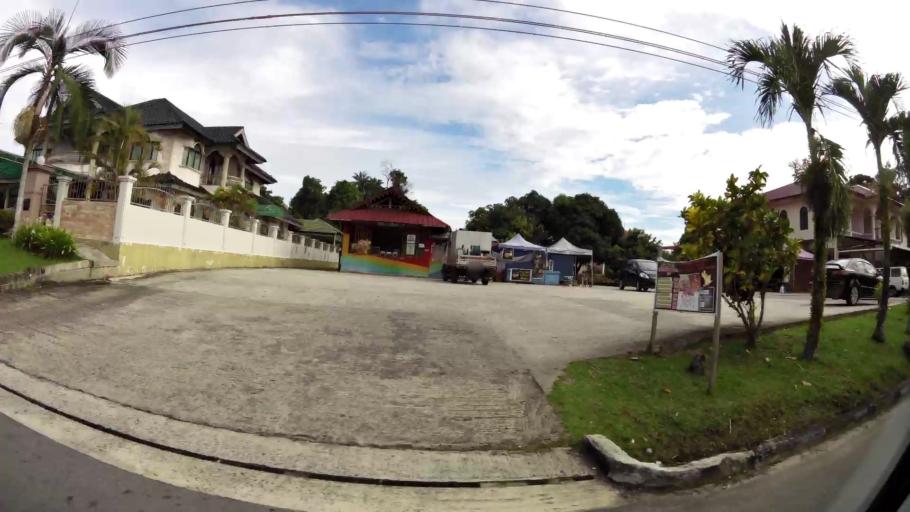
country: BN
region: Brunei and Muara
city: Bandar Seri Begawan
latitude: 4.8998
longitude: 114.8940
